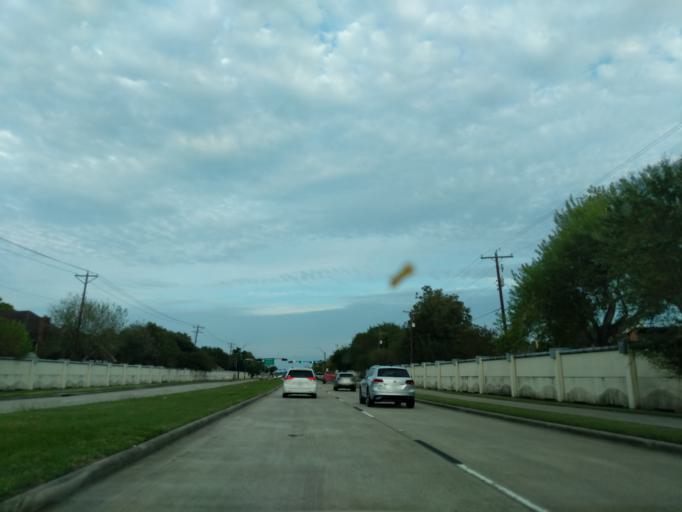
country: US
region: Texas
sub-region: Galveston County
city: Clear Lake Shores
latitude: 29.5249
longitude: -95.0593
